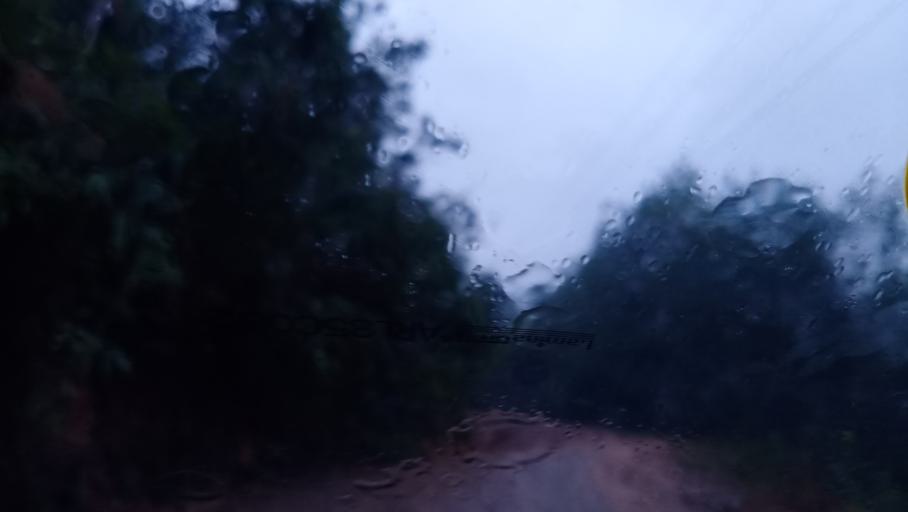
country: LA
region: Phongsali
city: Khoa
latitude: 21.1050
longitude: 102.3179
